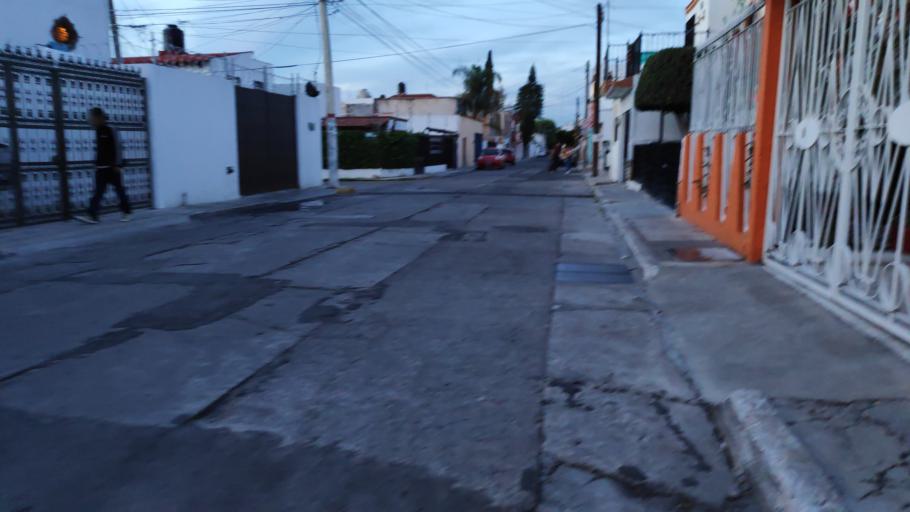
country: MX
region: Queretaro
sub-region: Queretaro
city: Santiago de Queretaro
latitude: 20.5828
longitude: -100.3829
